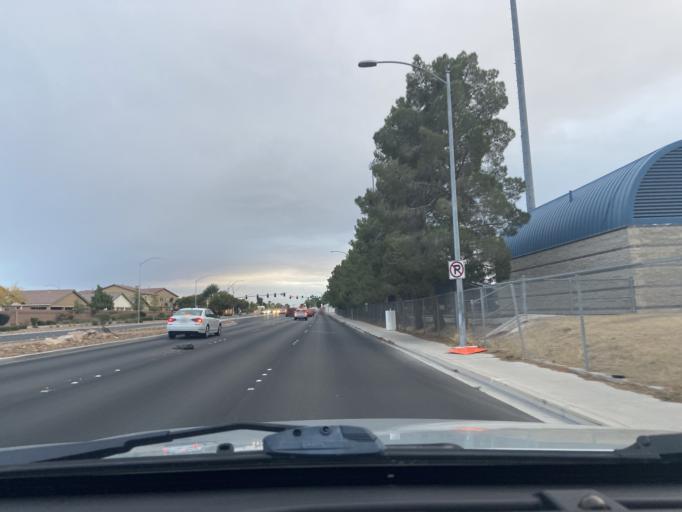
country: US
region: Nevada
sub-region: Clark County
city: North Las Vegas
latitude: 36.2338
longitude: -115.1803
